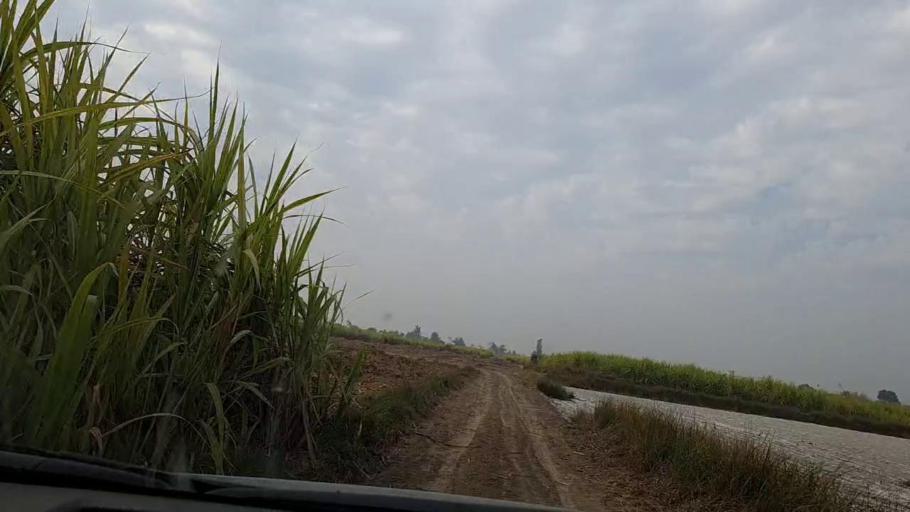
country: PK
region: Sindh
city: Daulatpur
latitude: 26.5647
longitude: 67.9806
